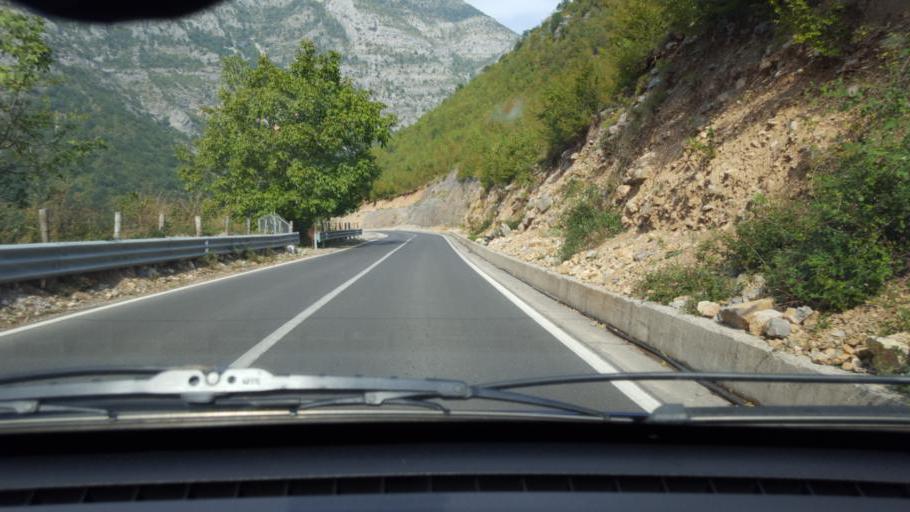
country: AL
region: Shkoder
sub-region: Rrethi i Malesia e Madhe
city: Kastrat
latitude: 42.4181
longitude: 19.5100
